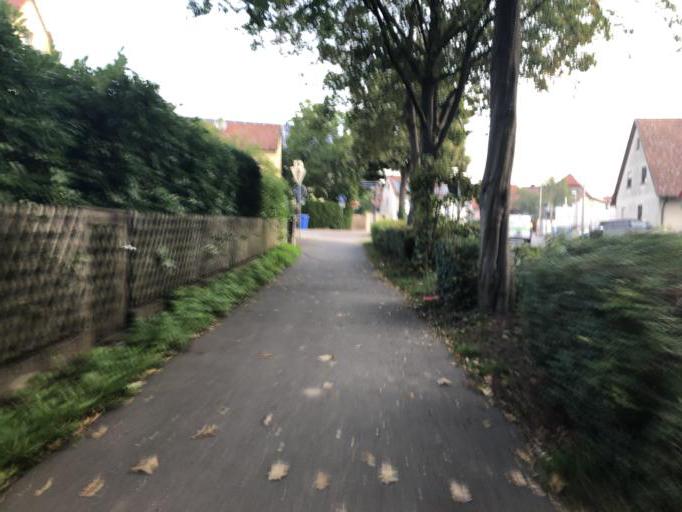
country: DE
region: Bavaria
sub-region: Regierungsbezirk Mittelfranken
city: Erlangen
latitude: 49.5884
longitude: 10.9598
